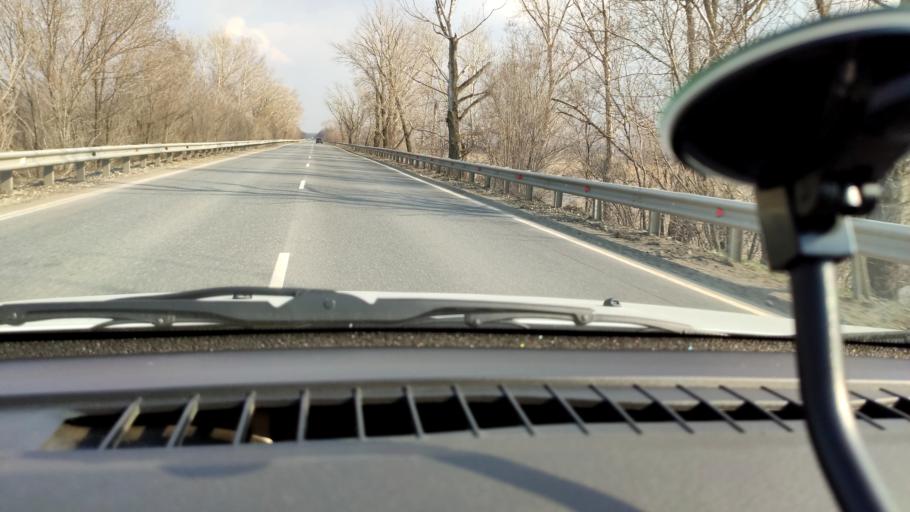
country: RU
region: Samara
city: Samara
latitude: 53.1063
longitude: 50.2428
